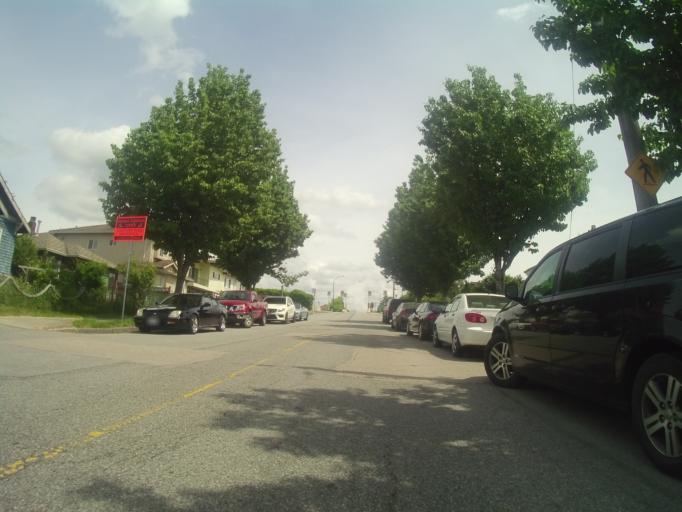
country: CA
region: British Columbia
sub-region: Fraser Valley Regional District
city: North Vancouver
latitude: 49.2774
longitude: -123.0329
